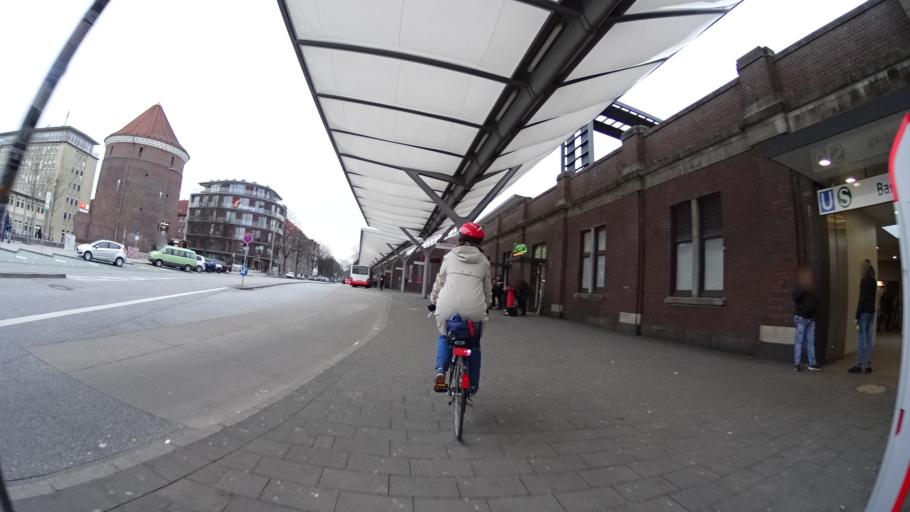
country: DE
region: Hamburg
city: Barmbek-Nord
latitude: 53.5867
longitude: 10.0458
